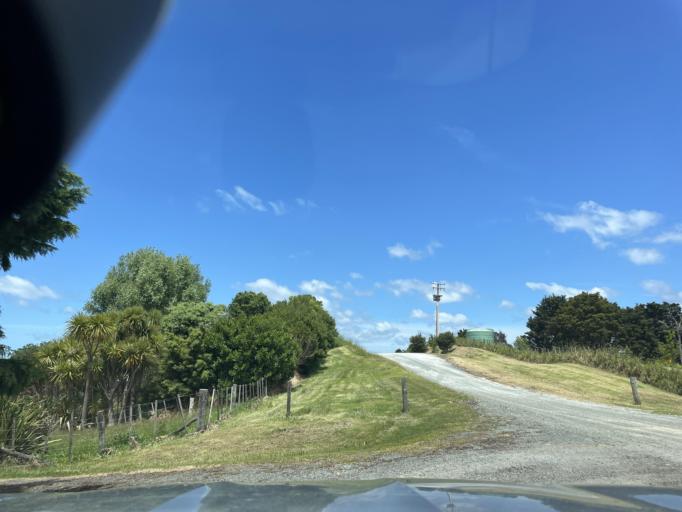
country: NZ
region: Auckland
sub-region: Auckland
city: Wellsford
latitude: -36.1728
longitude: 174.2727
